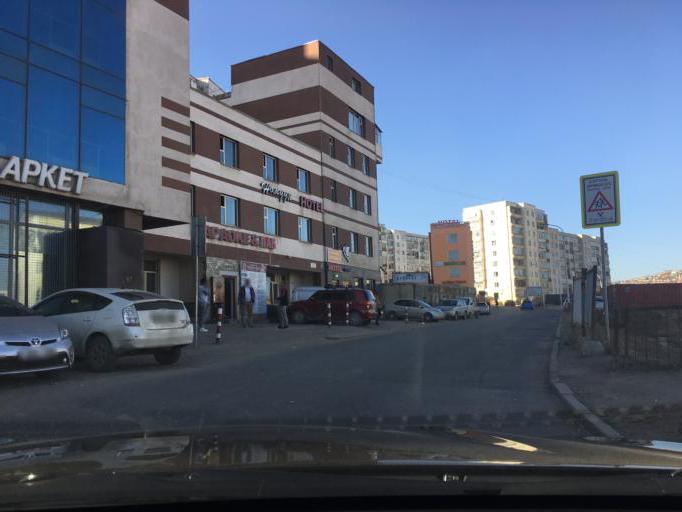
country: MN
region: Ulaanbaatar
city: Ulaanbaatar
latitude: 47.9255
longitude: 106.8827
